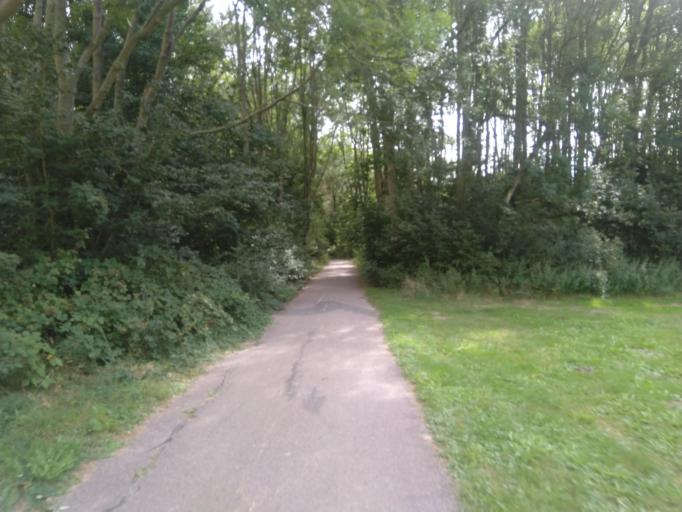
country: NL
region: North Holland
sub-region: Gemeente Zaanstad
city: Zaanstad
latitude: 52.3982
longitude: 4.7375
